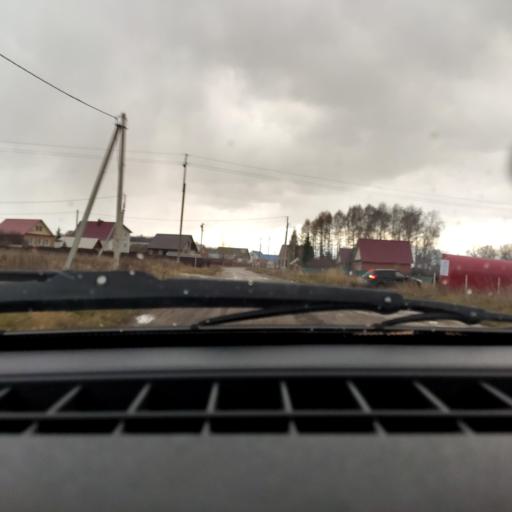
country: RU
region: Bashkortostan
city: Iglino
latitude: 54.7385
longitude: 56.3249
